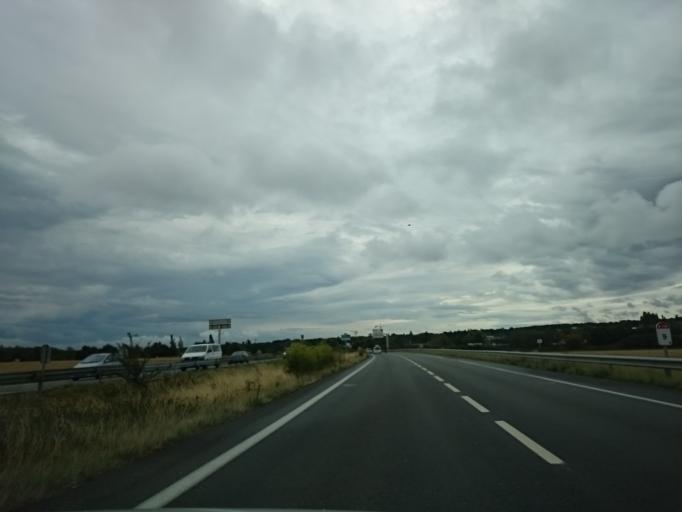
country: FR
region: Ile-de-France
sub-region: Departement de l'Essonne
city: Saclay
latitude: 48.7186
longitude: 2.1701
